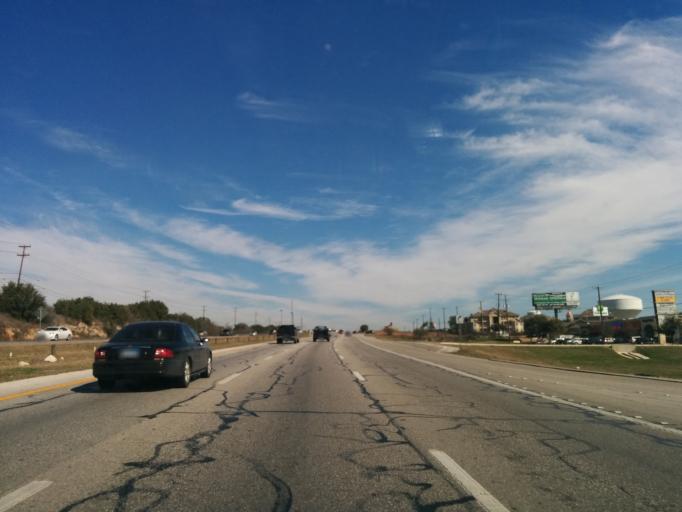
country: US
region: Texas
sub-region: Bexar County
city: Hollywood Park
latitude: 29.6215
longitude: -98.4647
